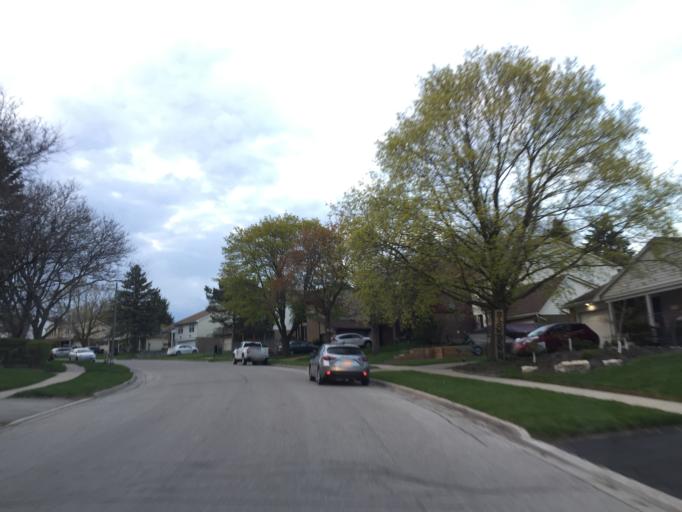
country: CA
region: Ontario
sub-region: Wellington County
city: Guelph
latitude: 43.5302
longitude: -80.2860
